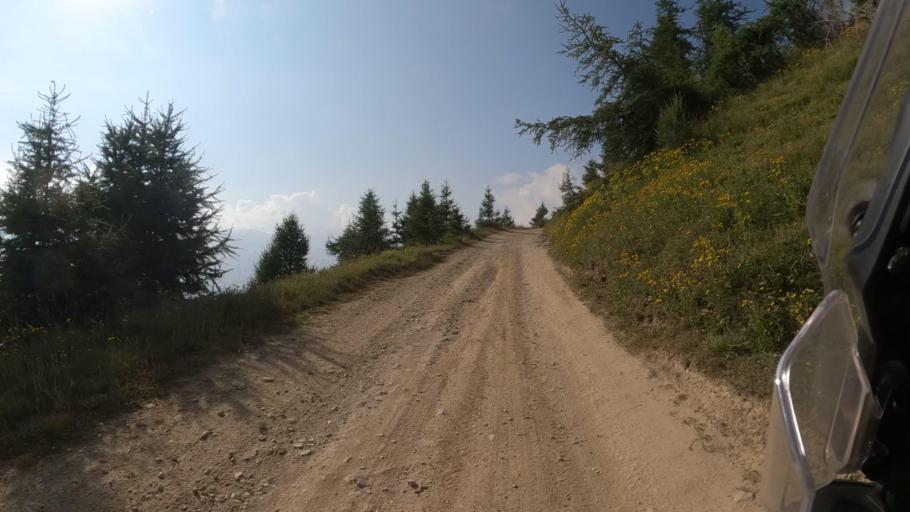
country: IT
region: Piedmont
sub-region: Provincia di Torino
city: Sauze d'Oulx
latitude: 45.0010
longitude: 6.8897
